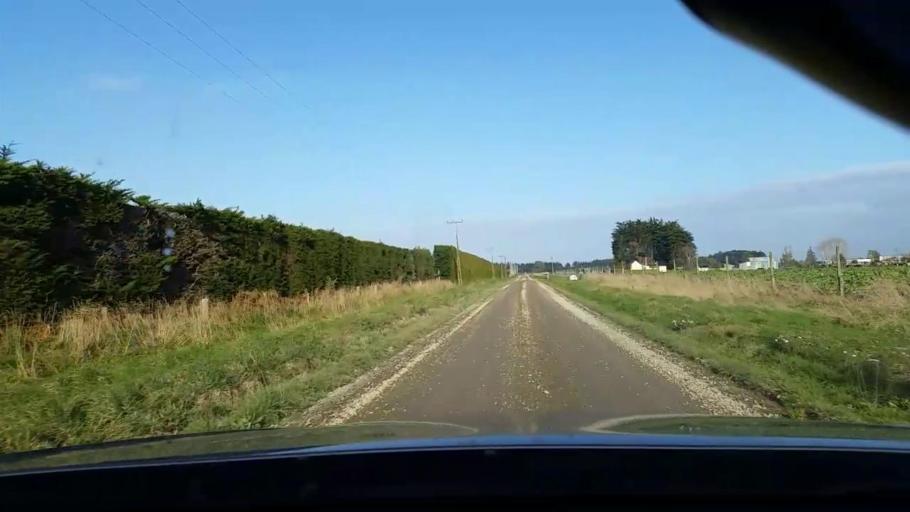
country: NZ
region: Southland
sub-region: Invercargill City
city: Invercargill
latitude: -46.2875
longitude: 168.2947
